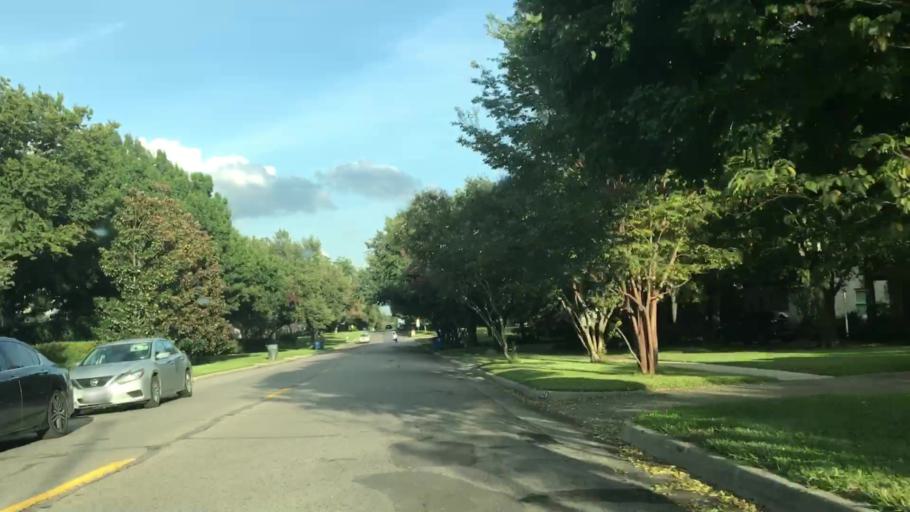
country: US
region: Texas
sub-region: Dallas County
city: Cockrell Hill
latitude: 32.7602
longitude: -96.8563
